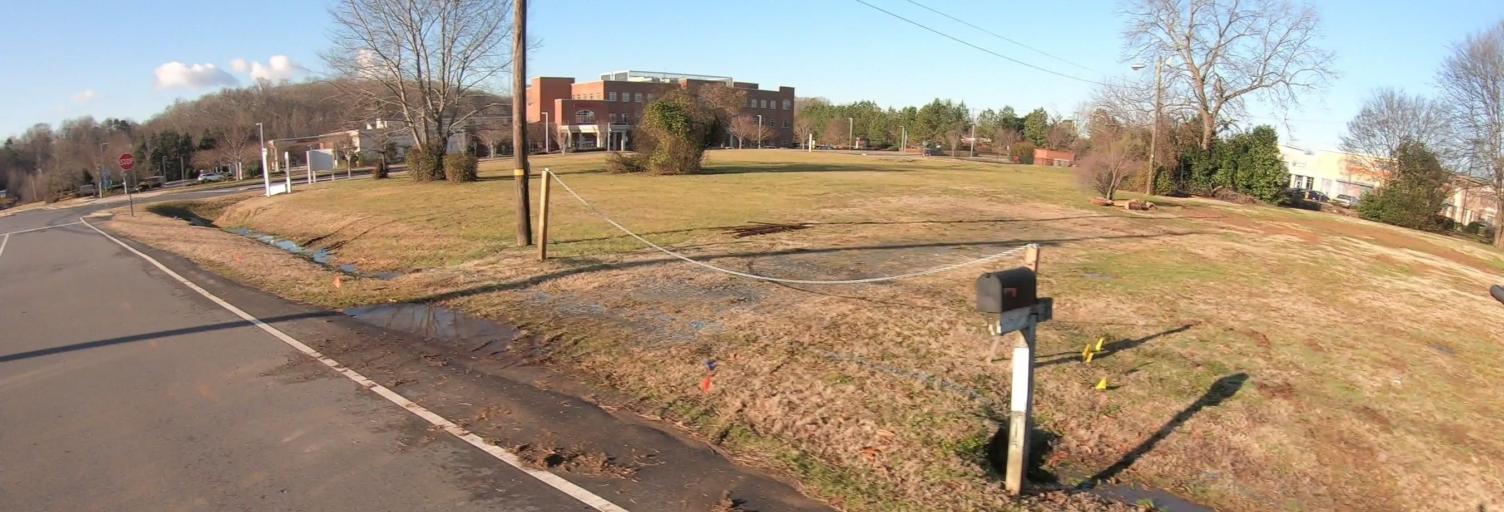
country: US
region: South Carolina
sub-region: York County
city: Lake Wylie
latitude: 35.1002
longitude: -80.9904
